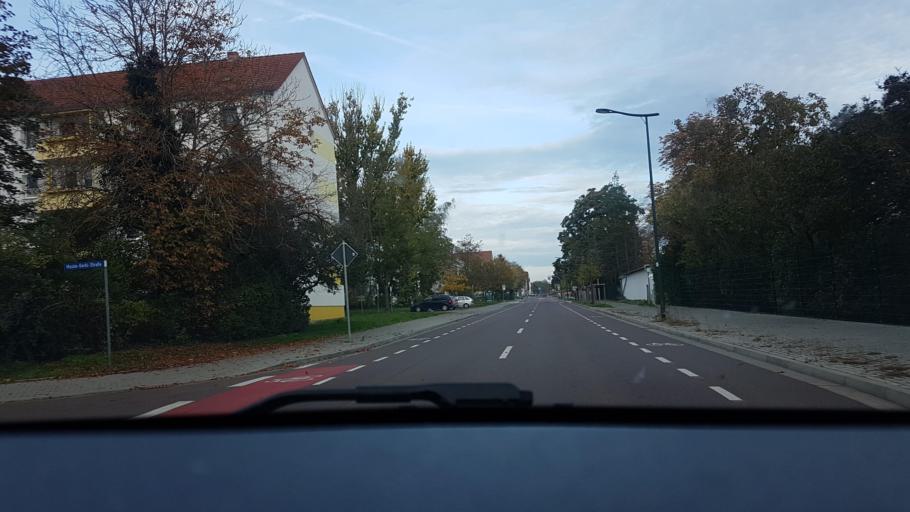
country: DE
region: Saxony-Anhalt
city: Bernburg
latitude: 51.7868
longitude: 11.7560
